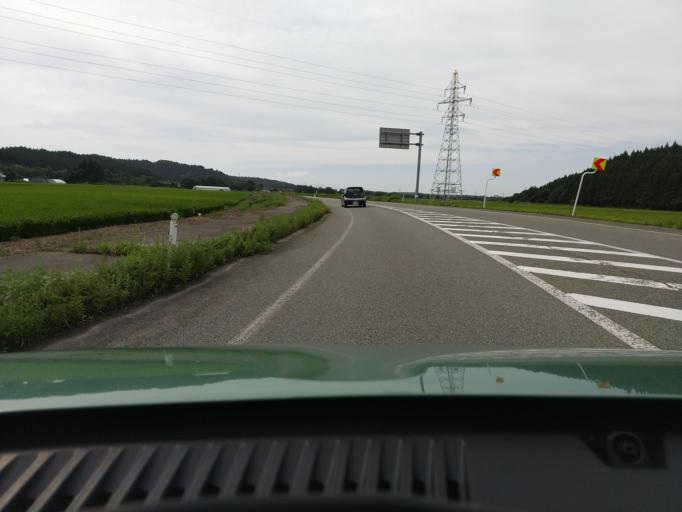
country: JP
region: Akita
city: Akita Shi
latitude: 39.7918
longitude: 140.1111
